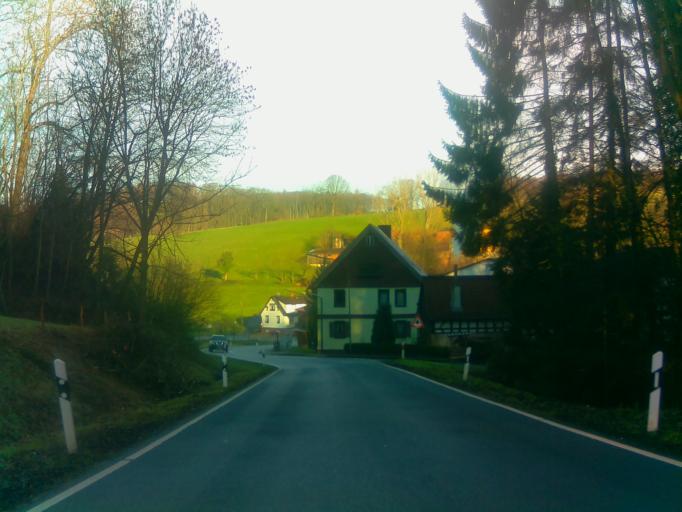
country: DE
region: Hesse
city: Reichelsheim
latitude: 49.6805
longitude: 8.8830
